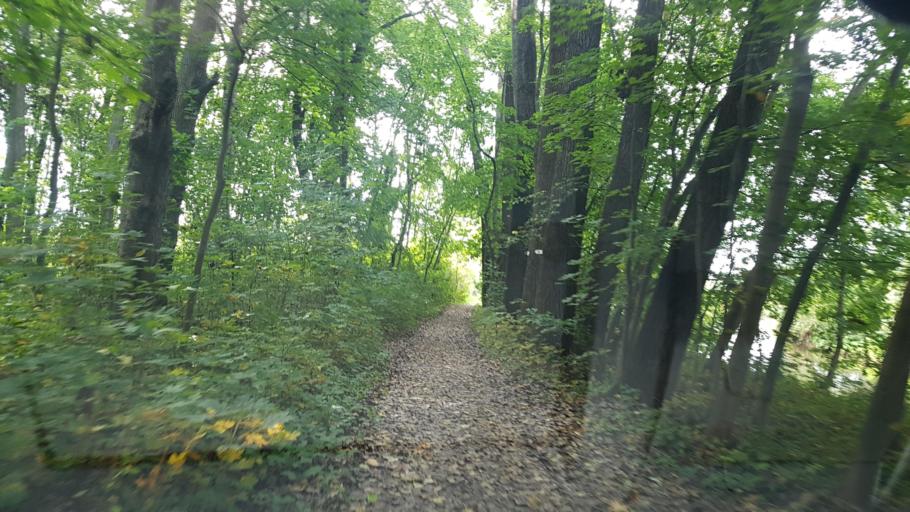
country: DE
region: Saxony
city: Pegau
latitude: 51.1598
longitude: 12.2625
